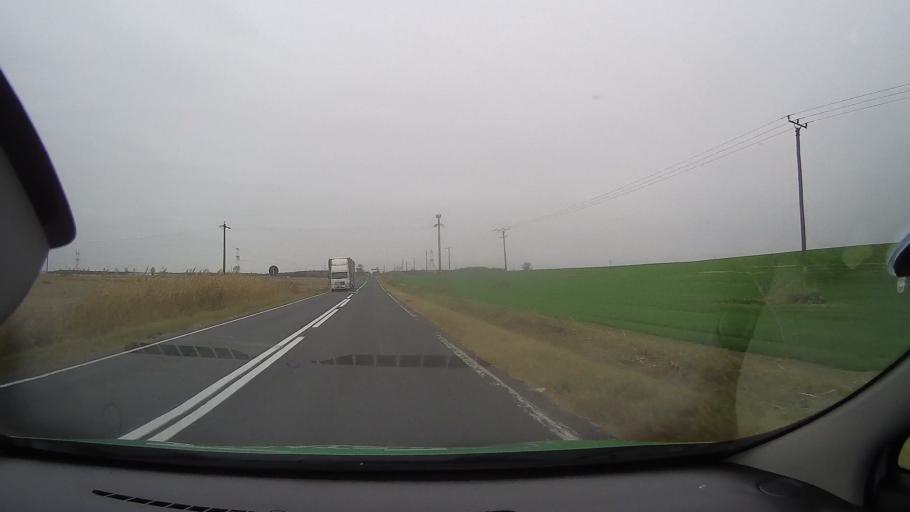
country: RO
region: Ialomita
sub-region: Comuna Gura Ialomitei
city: Gura Ialomitei
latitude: 44.6863
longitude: 27.7848
